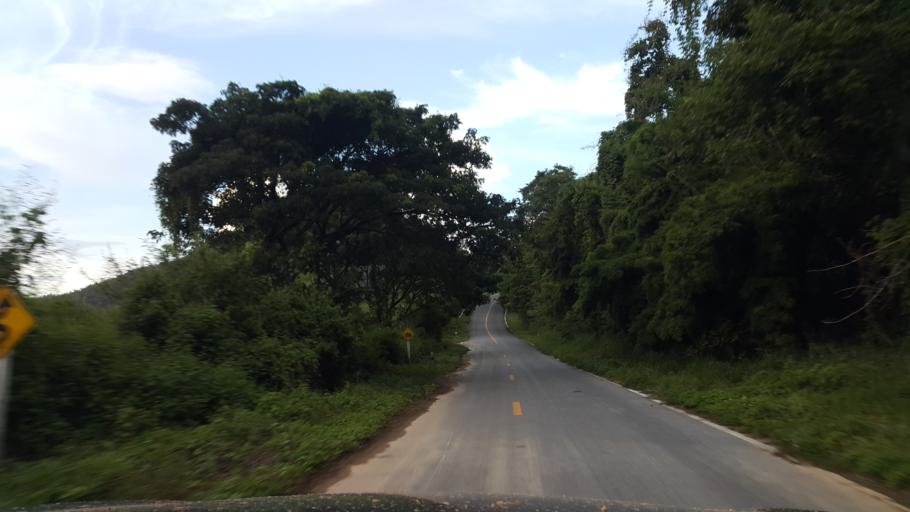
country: TH
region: Mae Hong Son
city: Mae Hi
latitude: 19.2438
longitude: 98.4529
